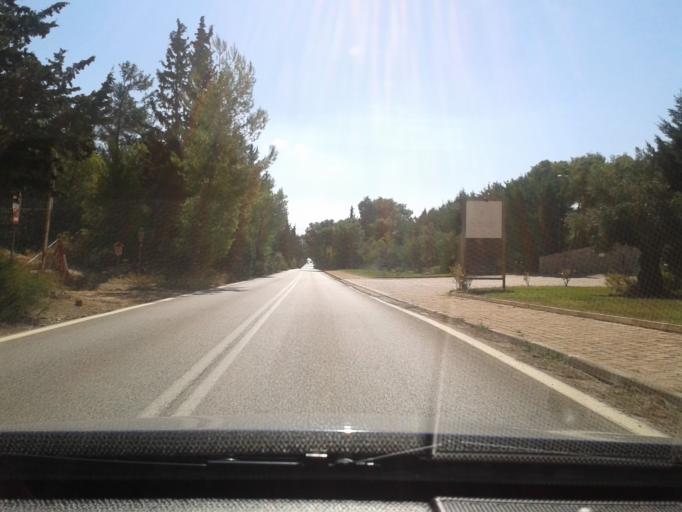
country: GR
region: Attica
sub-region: Nomarchia Anatolikis Attikis
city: Varybobi
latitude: 38.1243
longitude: 23.7959
